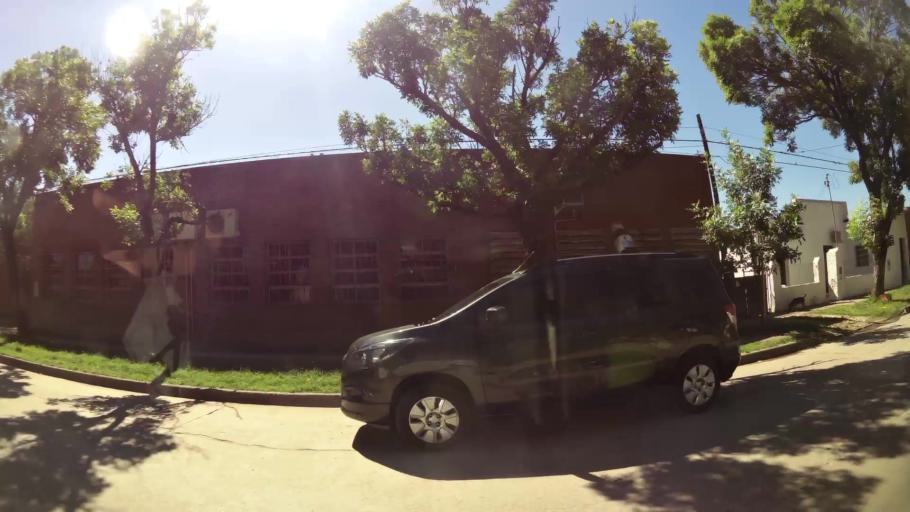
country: AR
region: Santa Fe
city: Esperanza
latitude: -31.4517
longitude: -60.9390
